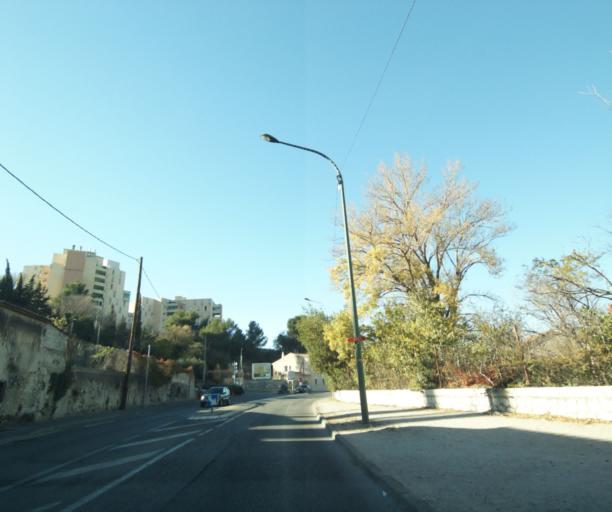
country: FR
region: Provence-Alpes-Cote d'Azur
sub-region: Departement des Bouches-du-Rhone
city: La Penne-sur-Huveaune
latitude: 43.2823
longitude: 5.5086
